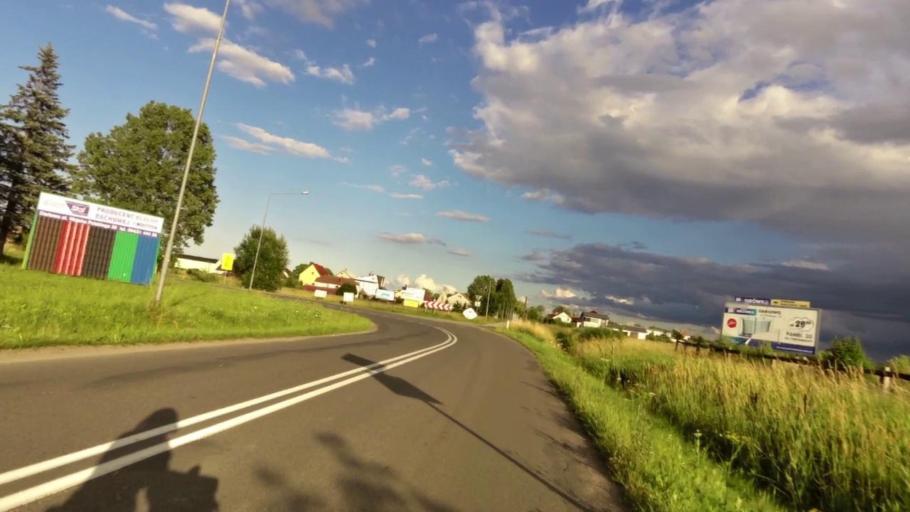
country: PL
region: West Pomeranian Voivodeship
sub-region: Powiat slawienski
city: Darlowo
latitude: 54.4134
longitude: 16.4049
